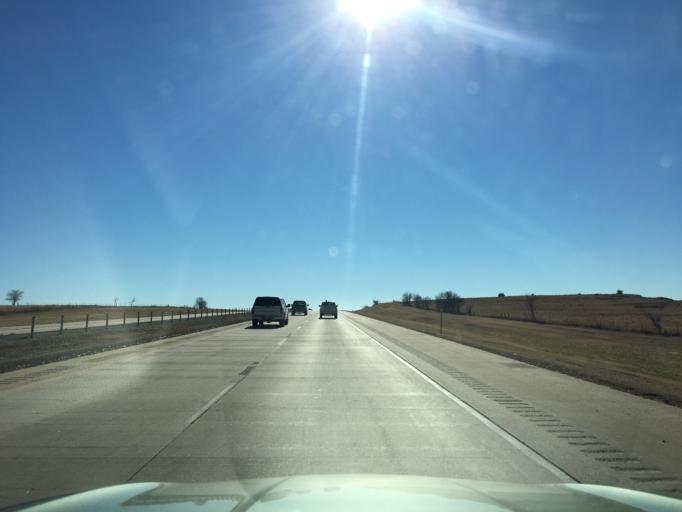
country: US
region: Oklahoma
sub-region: Noble County
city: Perry
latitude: 36.4558
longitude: -97.3271
